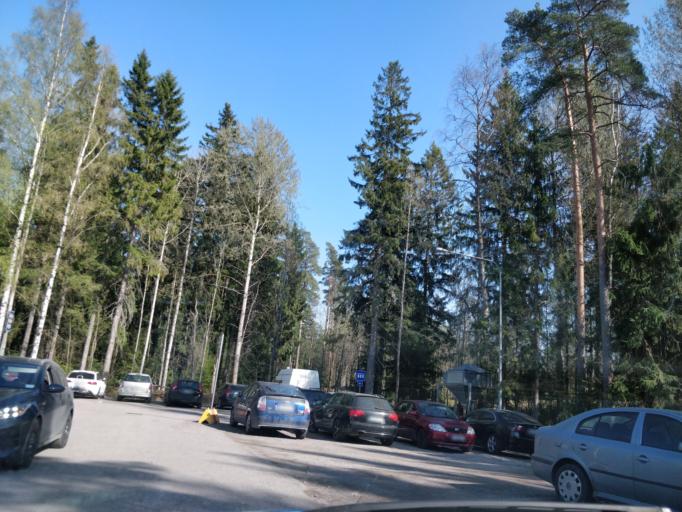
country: FI
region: Uusimaa
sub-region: Helsinki
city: Vantaa
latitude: 60.3145
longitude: 25.1124
